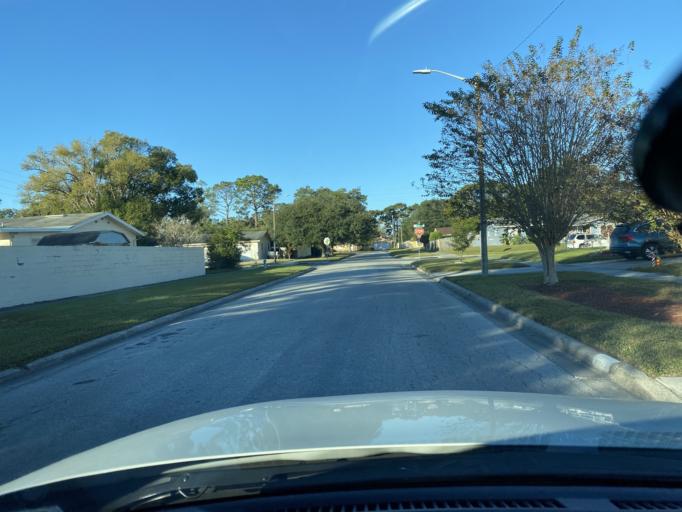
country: US
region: Florida
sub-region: Orange County
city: Azalea Park
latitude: 28.5291
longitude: -81.2982
